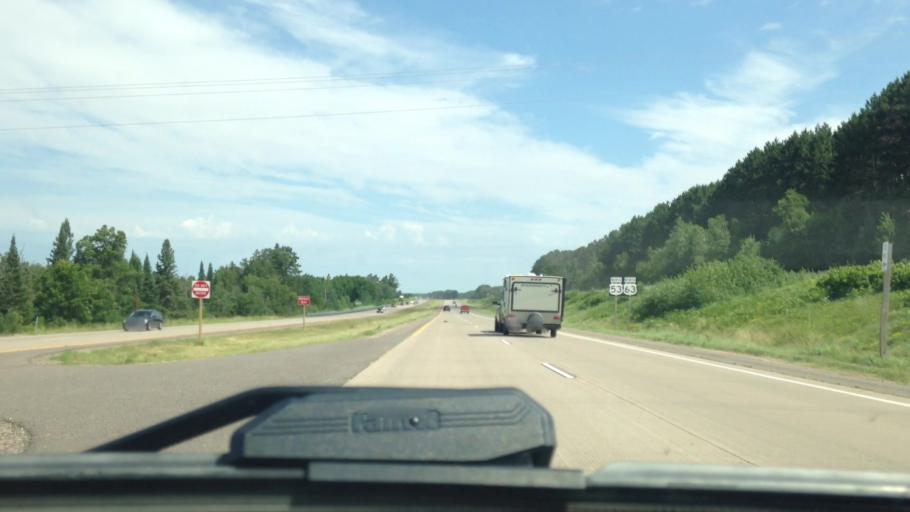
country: US
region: Wisconsin
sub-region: Washburn County
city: Spooner
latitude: 45.8716
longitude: -91.8302
